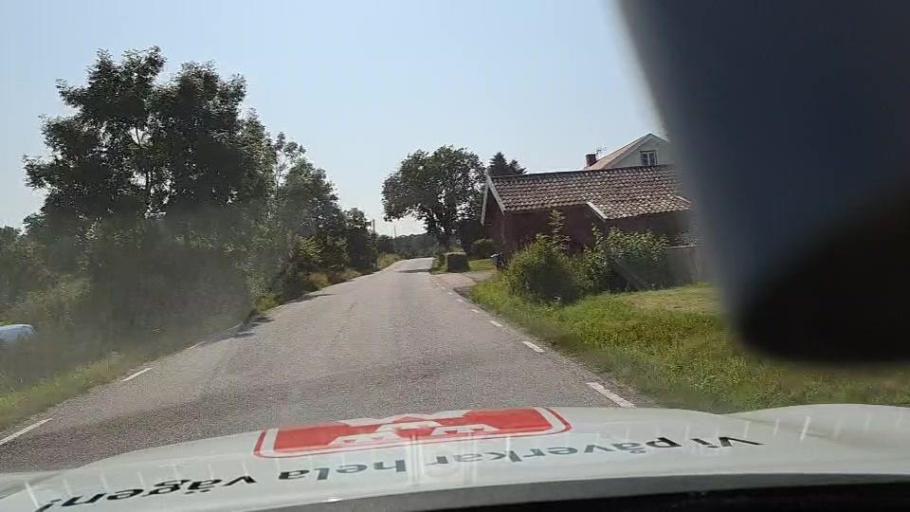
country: SE
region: Vaestra Goetaland
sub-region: Tjorns Kommun
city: Skaerhamn
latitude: 58.1245
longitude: 11.5455
